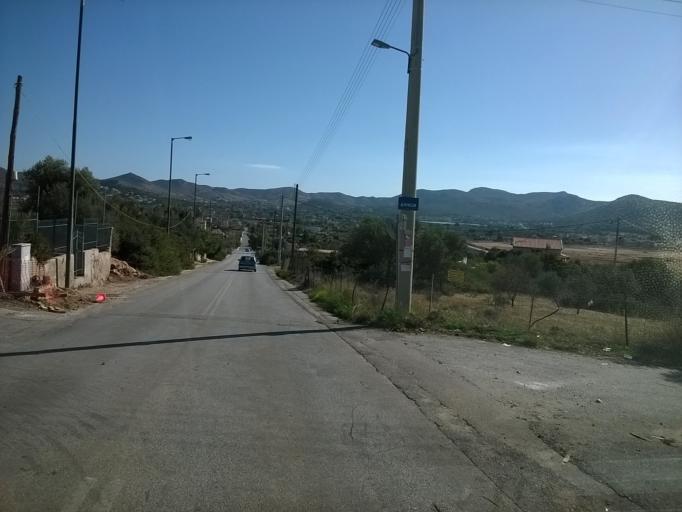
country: GR
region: Attica
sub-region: Nomarchia Anatolikis Attikis
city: Anavyssos
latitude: 37.7356
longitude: 23.9388
